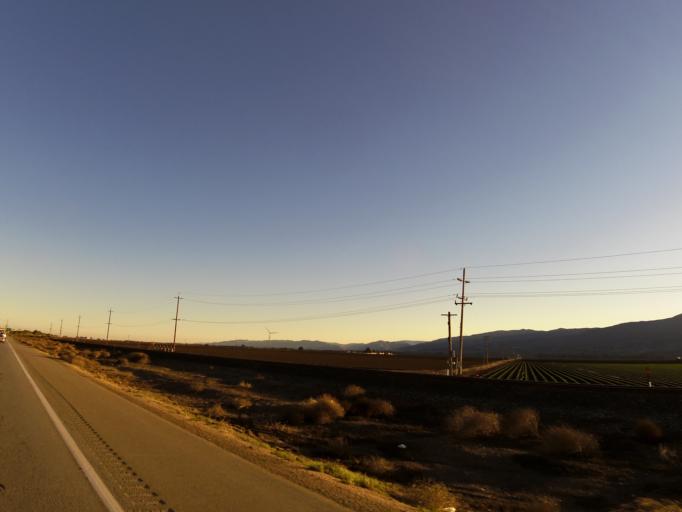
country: US
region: California
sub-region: Monterey County
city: Soledad
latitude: 36.4402
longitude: -121.3504
